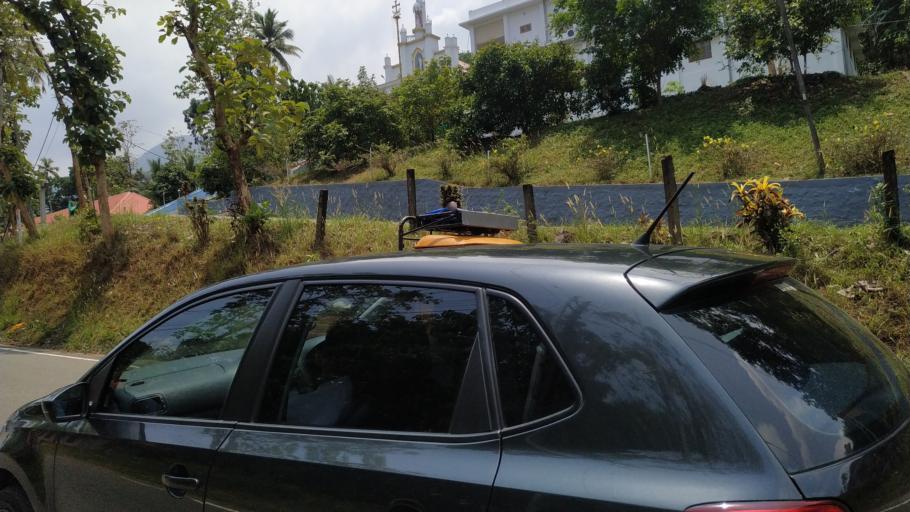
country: IN
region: Kerala
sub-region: Kottayam
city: Lalam
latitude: 9.8360
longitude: 76.7543
